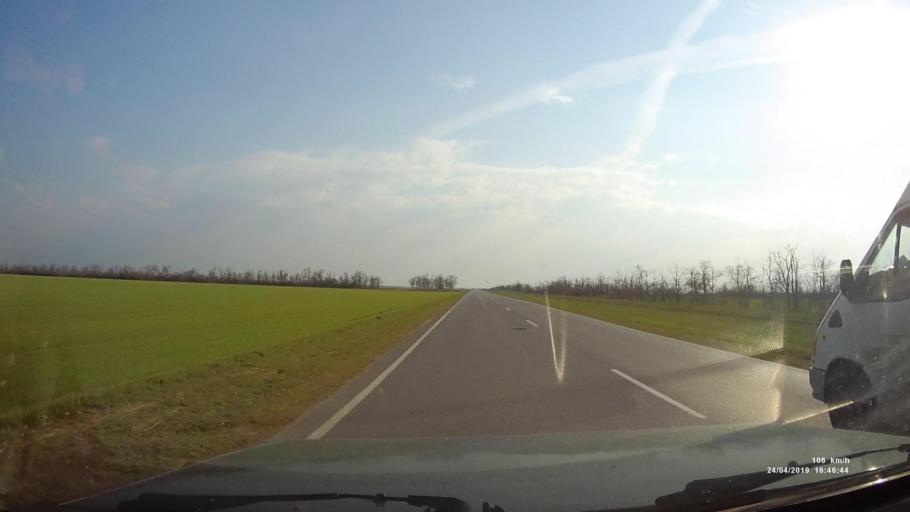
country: RU
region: Rostov
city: Proletarsk
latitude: 46.7533
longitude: 41.7972
